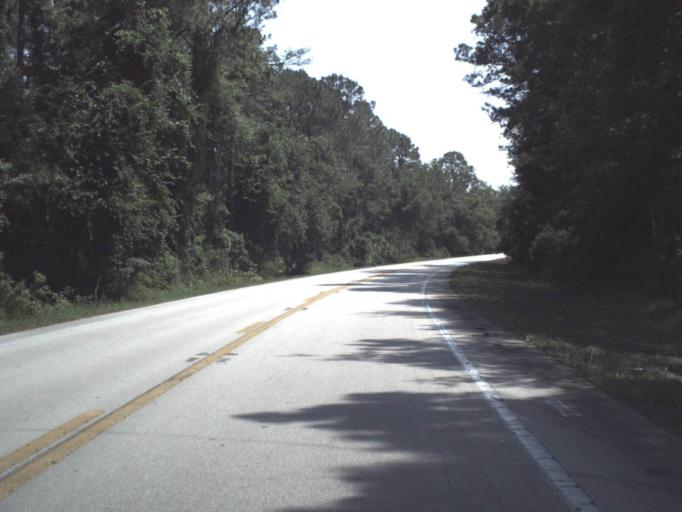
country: US
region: Florida
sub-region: Bradford County
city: Starke
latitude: 29.9764
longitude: -82.0164
